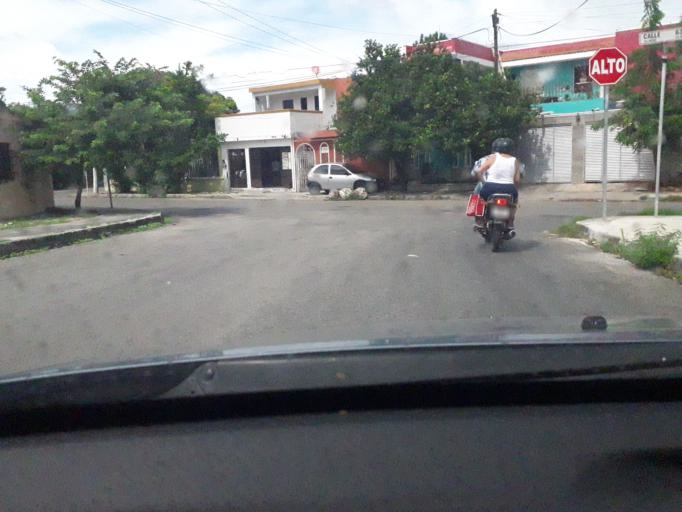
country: MX
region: Yucatan
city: Merida
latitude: 20.9644
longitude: -89.6562
